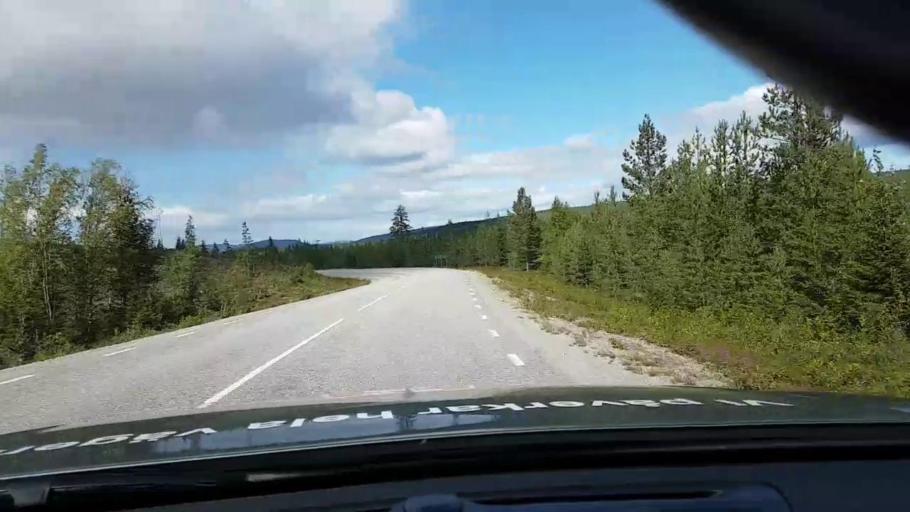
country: SE
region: Vaesternorrland
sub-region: OErnskoeldsviks Kommun
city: Bredbyn
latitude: 63.6771
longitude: 17.7917
